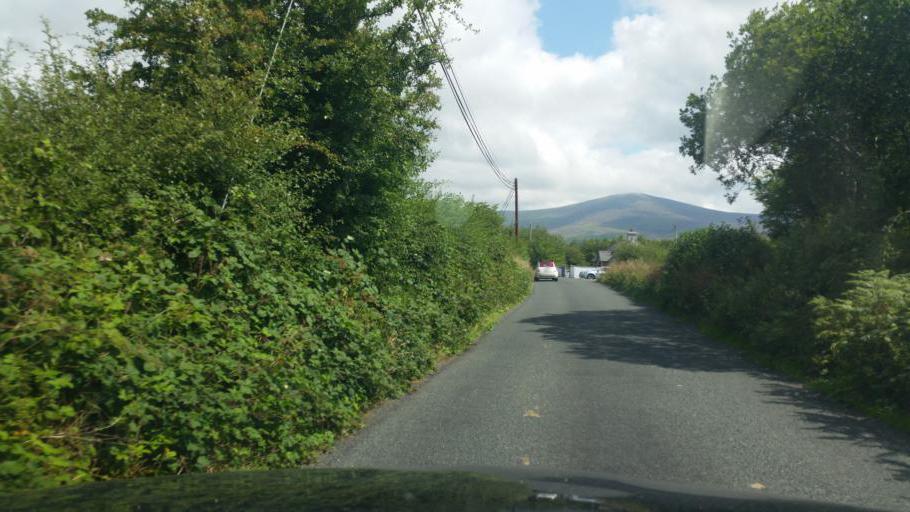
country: IE
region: Leinster
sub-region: Kilkenny
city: Graiguenamanagh
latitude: 52.6076
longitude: -6.8830
